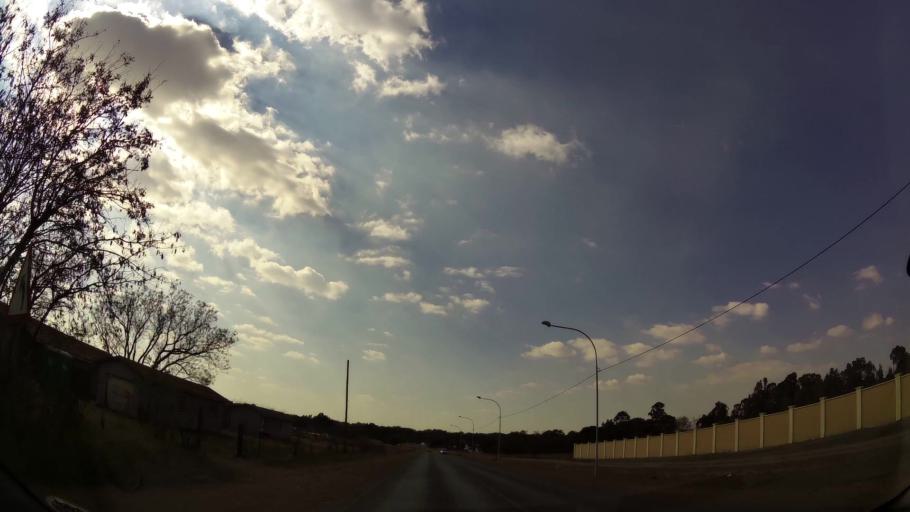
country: ZA
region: Gauteng
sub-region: Ekurhuleni Metropolitan Municipality
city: Benoni
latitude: -26.1023
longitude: 28.3501
